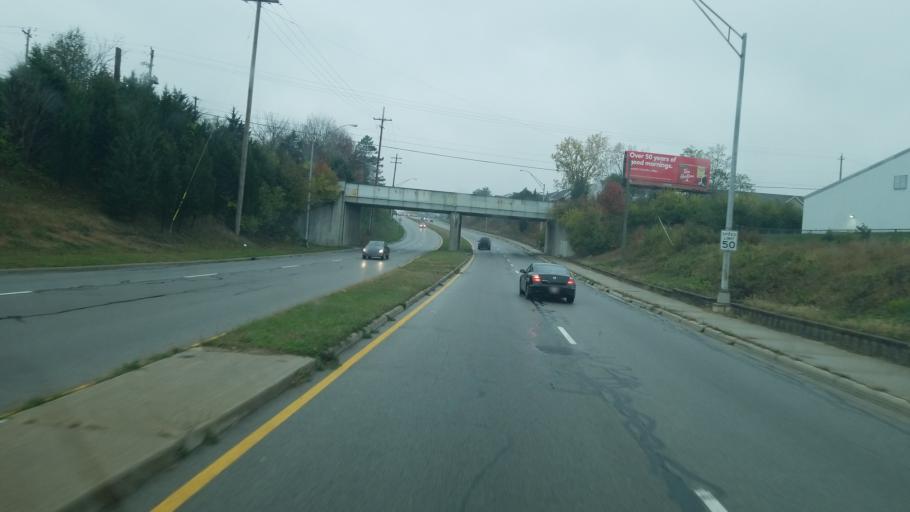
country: US
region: Ohio
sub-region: Franklin County
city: Worthington
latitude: 40.0527
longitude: -83.0431
